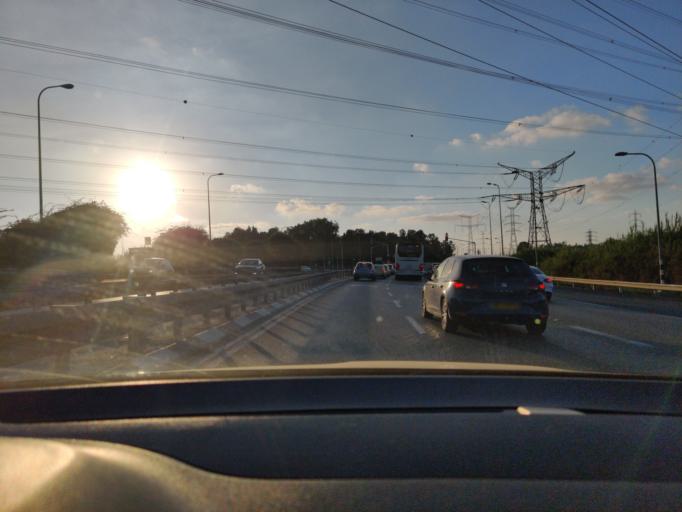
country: IL
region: Haifa
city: Hadera
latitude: 32.4470
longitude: 34.9443
